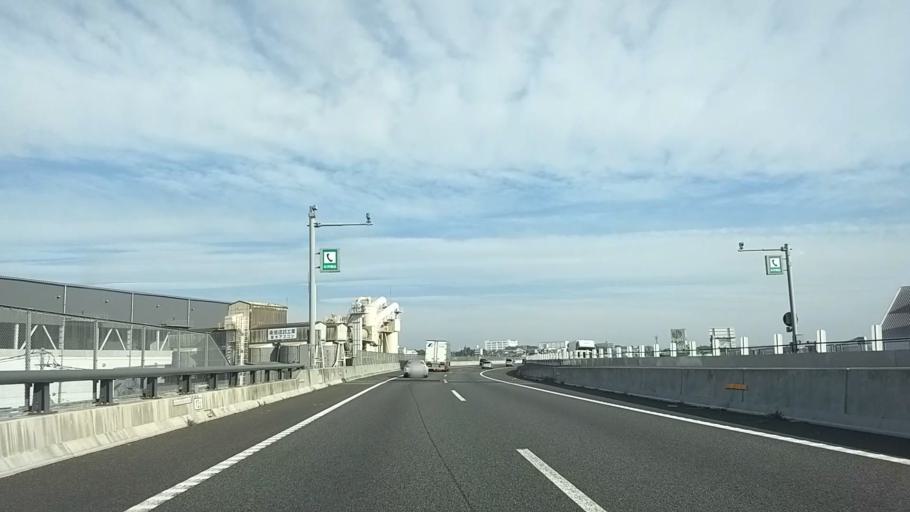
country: JP
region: Kanagawa
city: Atsugi
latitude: 35.4556
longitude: 139.3728
